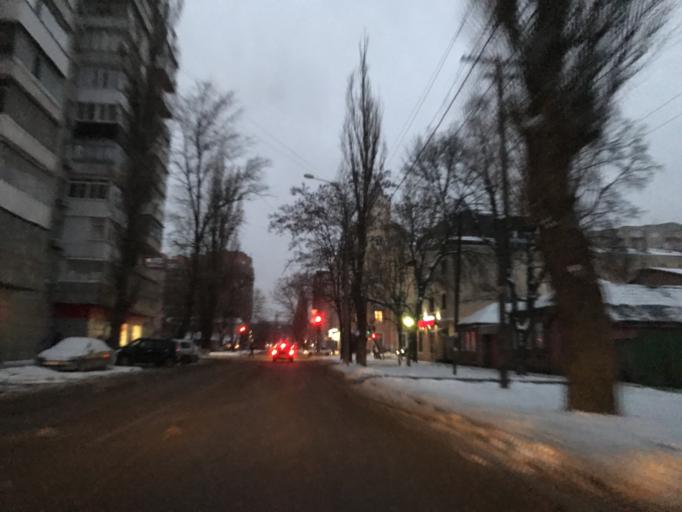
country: RU
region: Rostov
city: Imeni Chkalova
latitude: 47.2497
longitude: 39.7692
